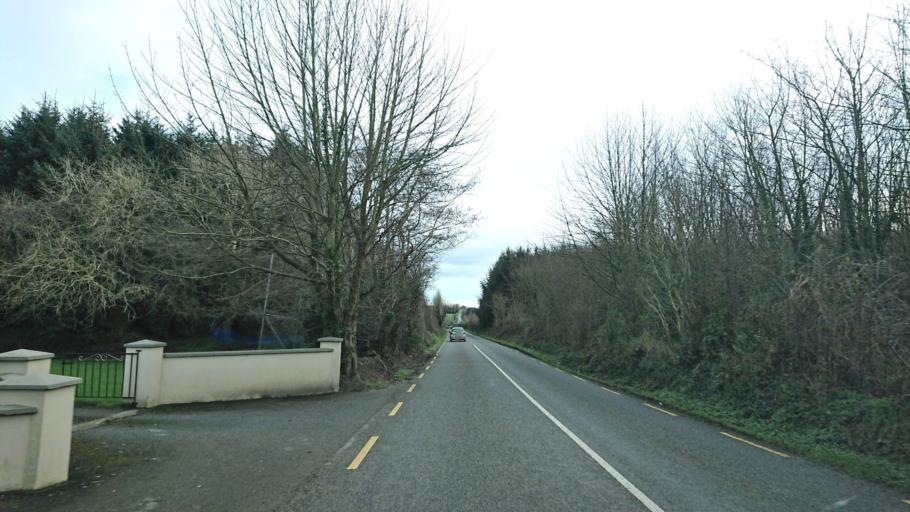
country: IE
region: Munster
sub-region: Waterford
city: Dunmore East
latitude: 52.2425
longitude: -6.8945
